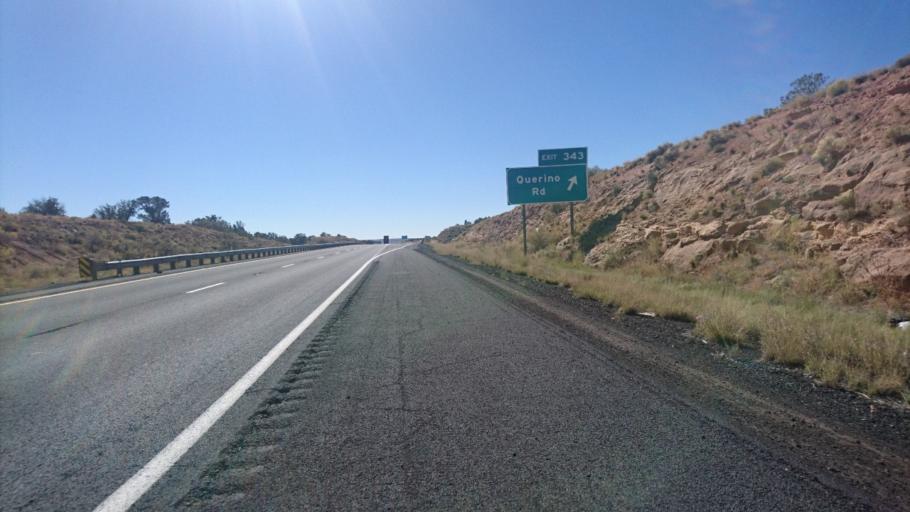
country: US
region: Arizona
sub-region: Apache County
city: Houck
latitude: 35.2635
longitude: -109.2747
